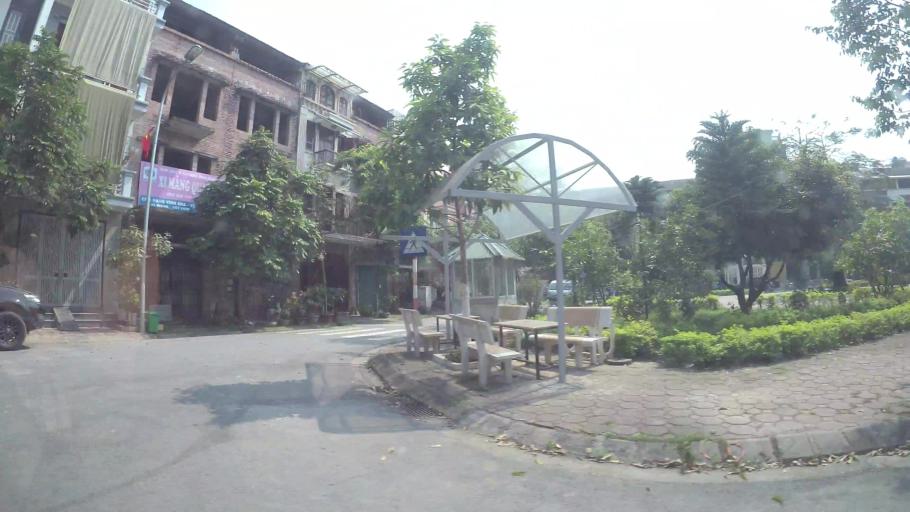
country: VN
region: Ha Noi
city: Ha Dong
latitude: 20.9729
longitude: 105.7976
